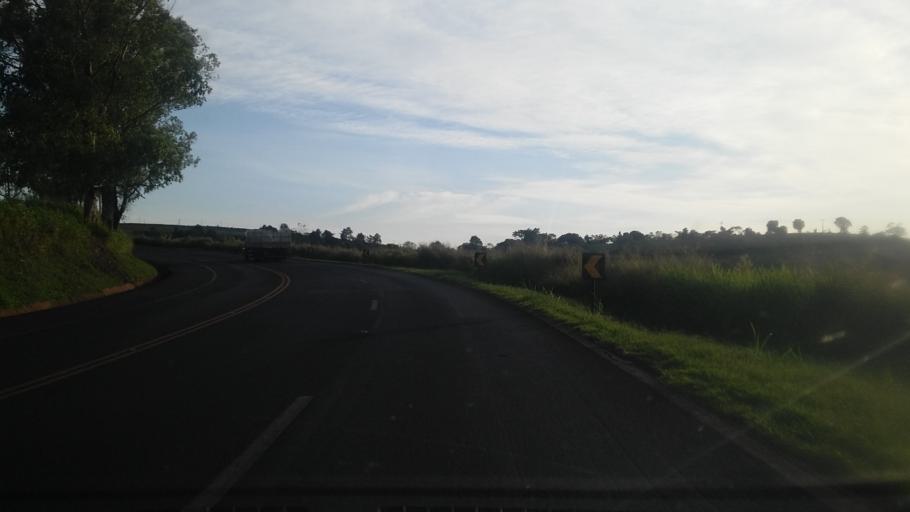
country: BR
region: Parana
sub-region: Bandeirantes
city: Bandeirantes
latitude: -23.1799
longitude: -50.6243
